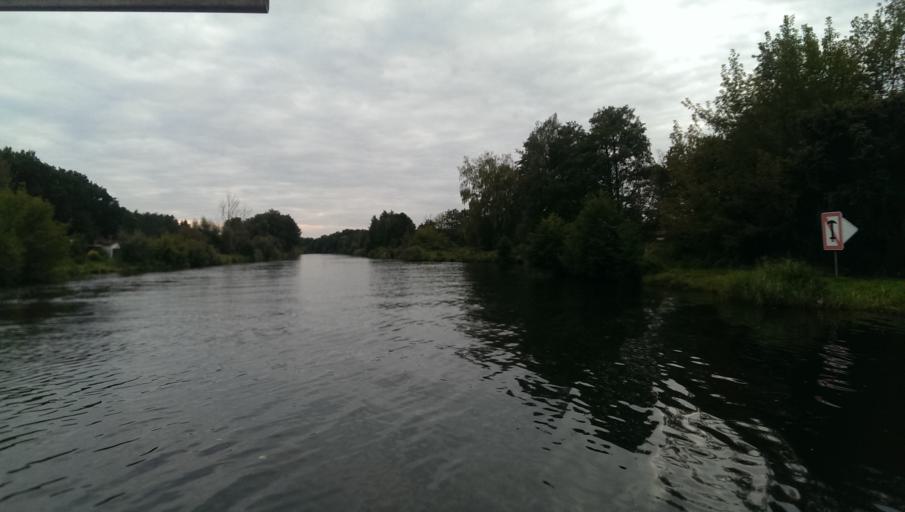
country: DE
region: Brandenburg
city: Oranienburg
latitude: 52.7223
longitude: 13.2500
